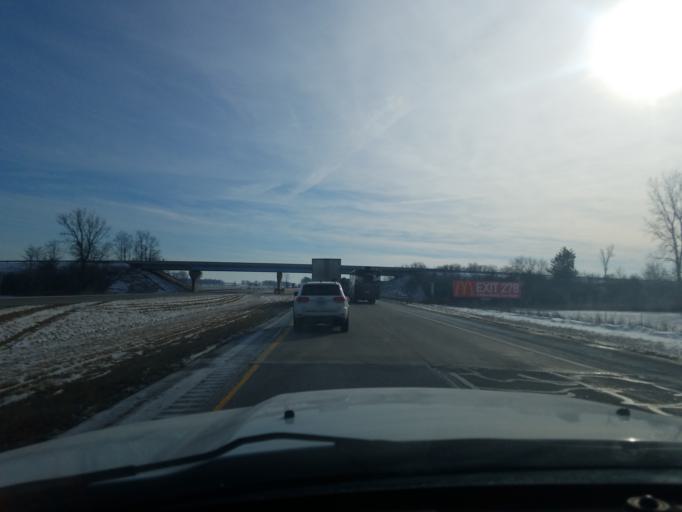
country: US
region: Indiana
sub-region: Huntington County
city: Markle
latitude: 40.7867
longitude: -85.3838
